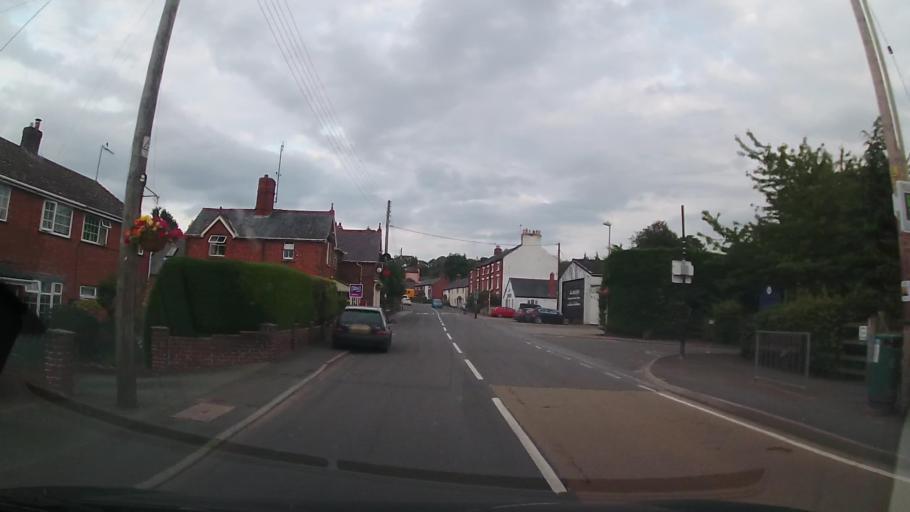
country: GB
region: England
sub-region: Shropshire
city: Great Ness
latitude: 52.7939
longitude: -2.9021
